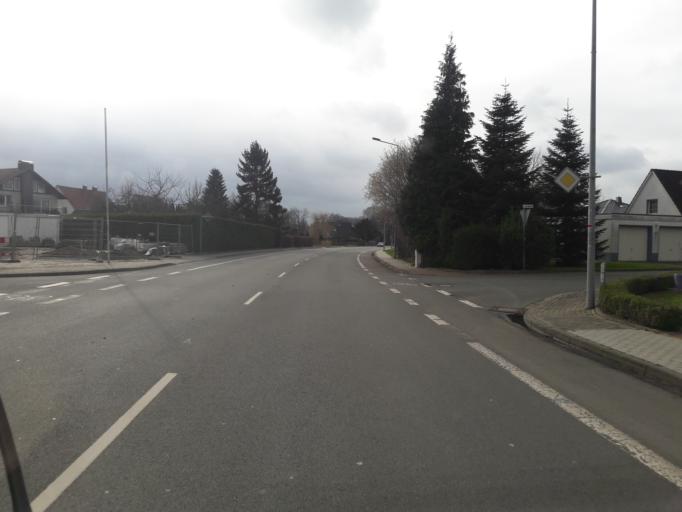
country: DE
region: North Rhine-Westphalia
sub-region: Regierungsbezirk Detmold
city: Hille
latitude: 52.3188
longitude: 8.8282
